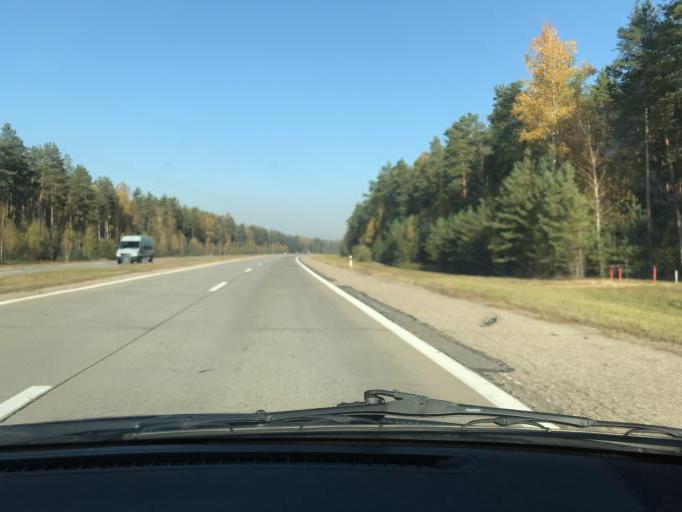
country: BY
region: Minsk
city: Uzda
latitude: 53.4015
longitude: 27.4810
